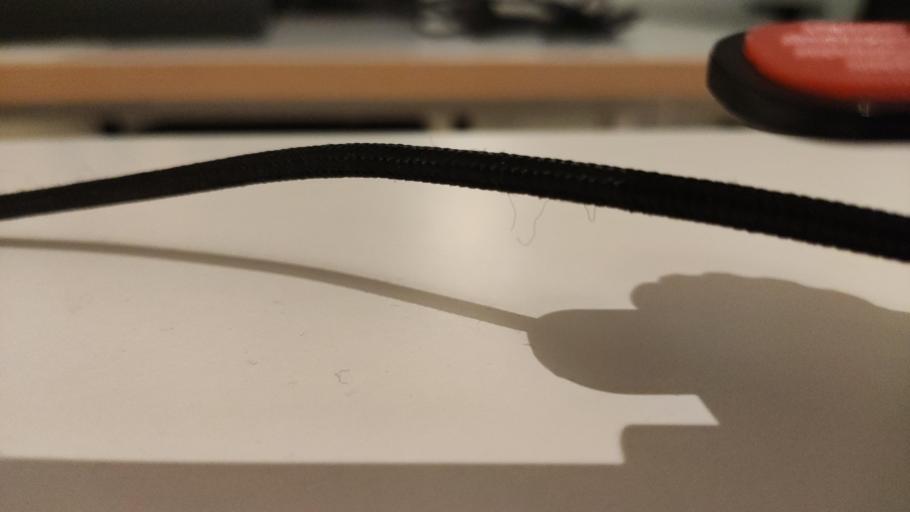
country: RU
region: Moskovskaya
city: Kurovskoye
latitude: 55.5719
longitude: 38.8855
